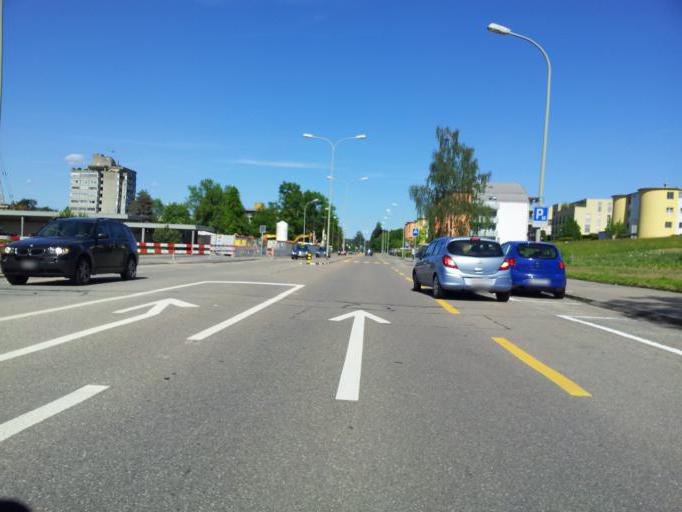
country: CH
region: Zurich
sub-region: Bezirk Dietikon
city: Schlieren / Spital
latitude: 47.3927
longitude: 8.4298
